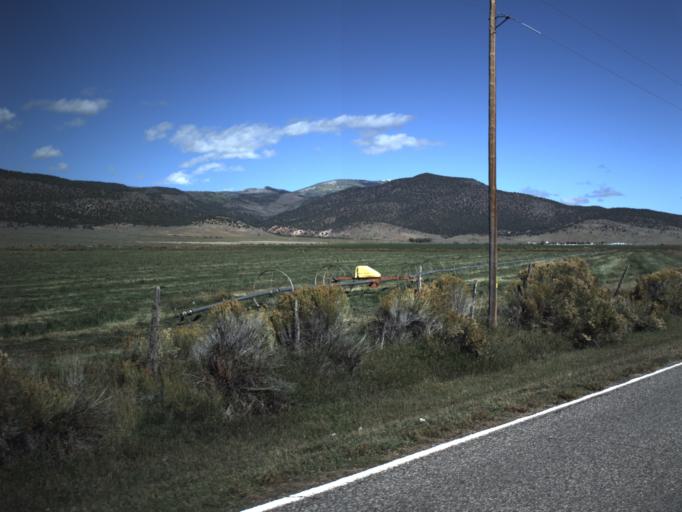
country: US
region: Utah
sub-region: Sevier County
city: Monroe
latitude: 38.4595
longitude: -111.9101
